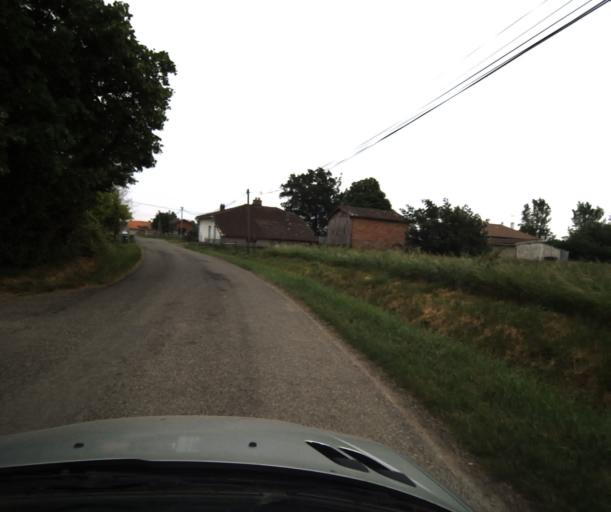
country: FR
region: Midi-Pyrenees
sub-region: Departement du Tarn-et-Garonne
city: Saint-Nicolas-de-la-Grave
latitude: 44.0497
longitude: 1.0125
